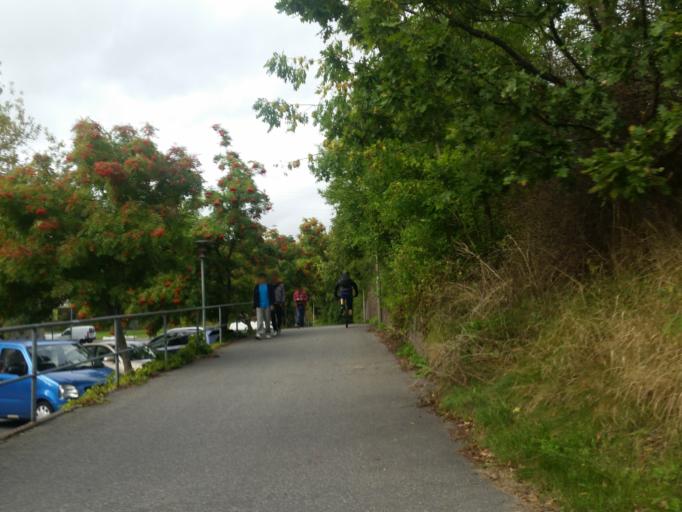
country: SE
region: Stockholm
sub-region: Stockholms Kommun
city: Arsta
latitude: 59.2587
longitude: 18.0992
